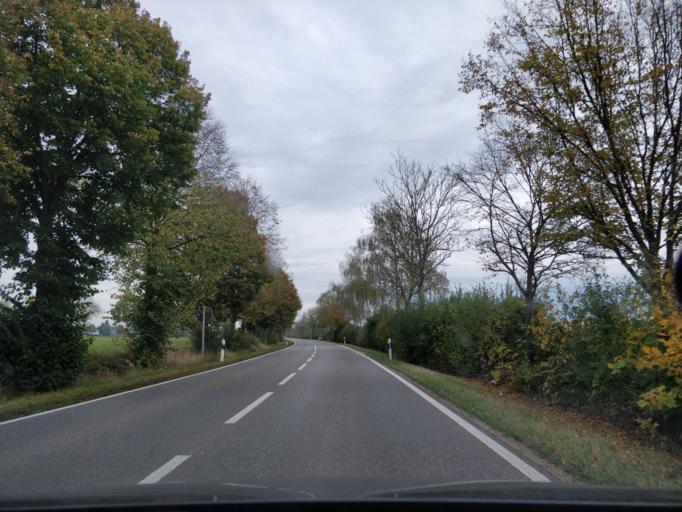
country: DE
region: Bavaria
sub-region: Swabia
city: Konigsbrunn
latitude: 48.2521
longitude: 10.8831
